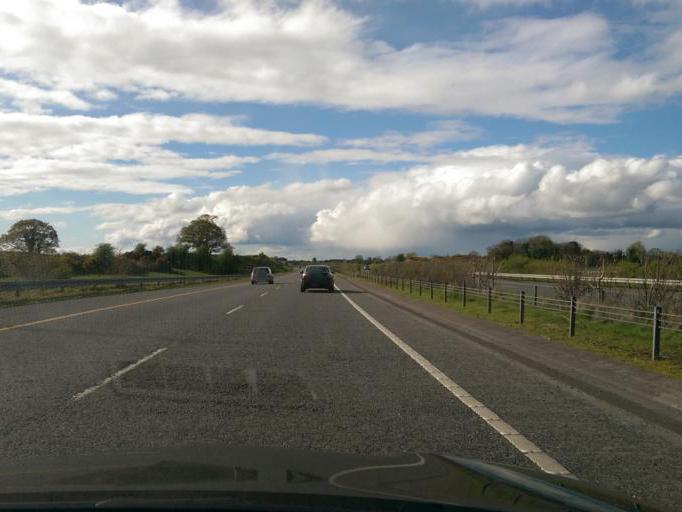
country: IE
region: Leinster
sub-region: An Mhi
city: Longwood
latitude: 53.4291
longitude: -6.9903
